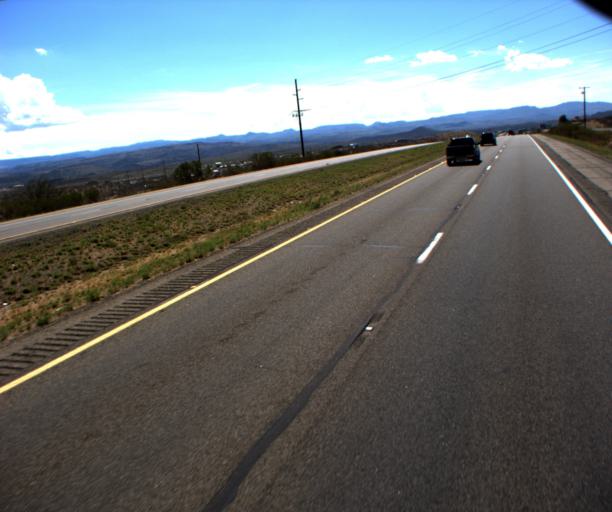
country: US
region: Arizona
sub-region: Yavapai County
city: Spring Valley
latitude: 34.3414
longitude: -112.1372
